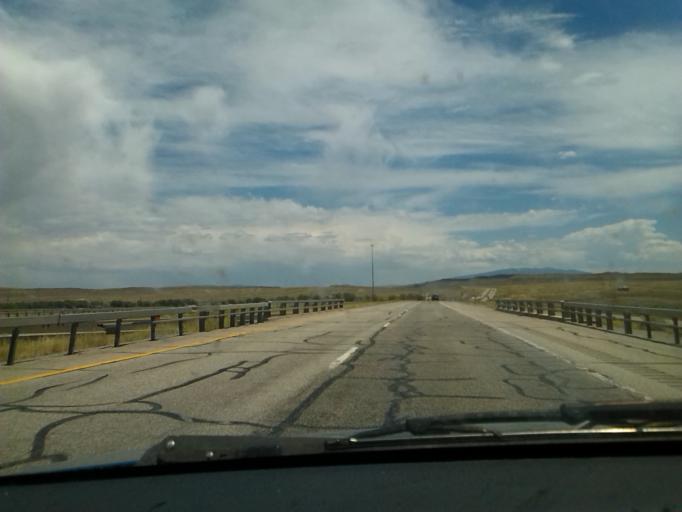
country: US
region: Wyoming
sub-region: Carbon County
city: Rawlins
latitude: 41.7541
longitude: -106.9615
